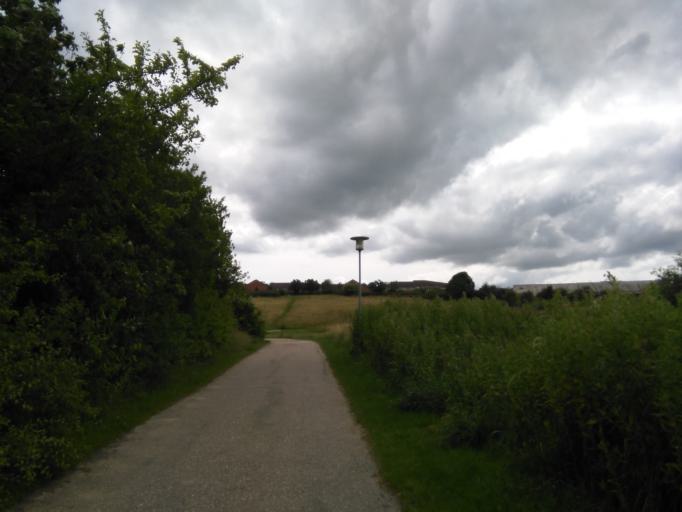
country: DK
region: Central Jutland
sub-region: Arhus Kommune
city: Arhus
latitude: 56.1099
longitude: 10.1999
